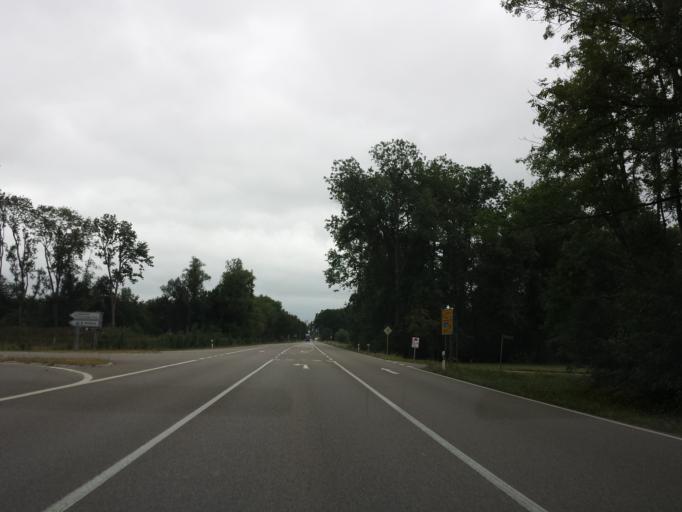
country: DE
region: Bavaria
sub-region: Swabia
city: Guenzburg
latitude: 48.4696
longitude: 10.2850
